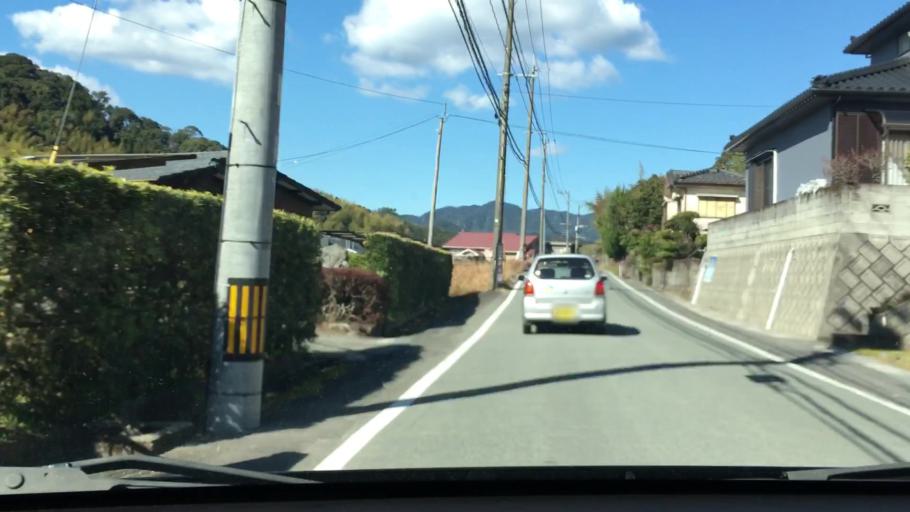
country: JP
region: Kagoshima
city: Ijuin
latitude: 31.6846
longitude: 130.4690
